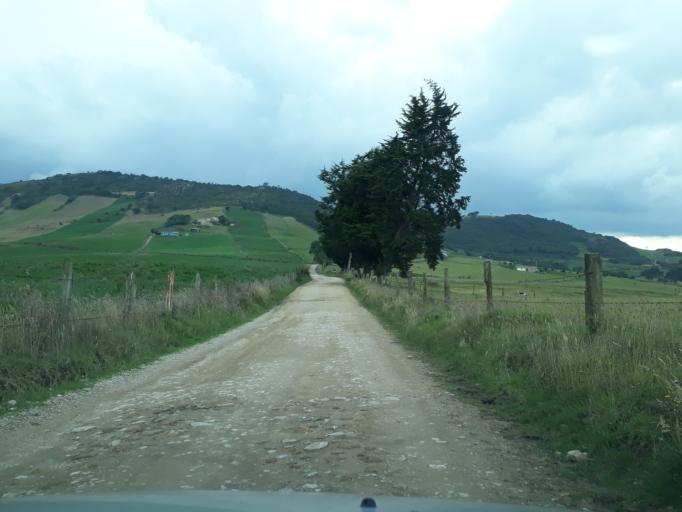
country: CO
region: Cundinamarca
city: Villapinzon
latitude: 5.2367
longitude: -73.6683
